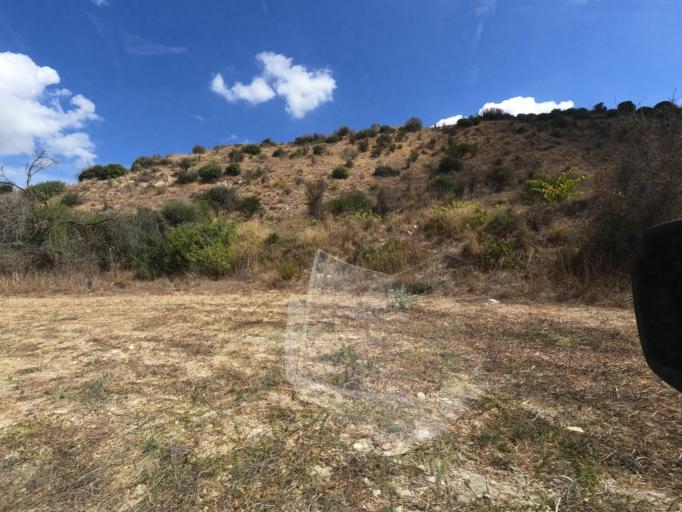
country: CY
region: Pafos
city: Mesogi
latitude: 34.8313
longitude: 32.5462
